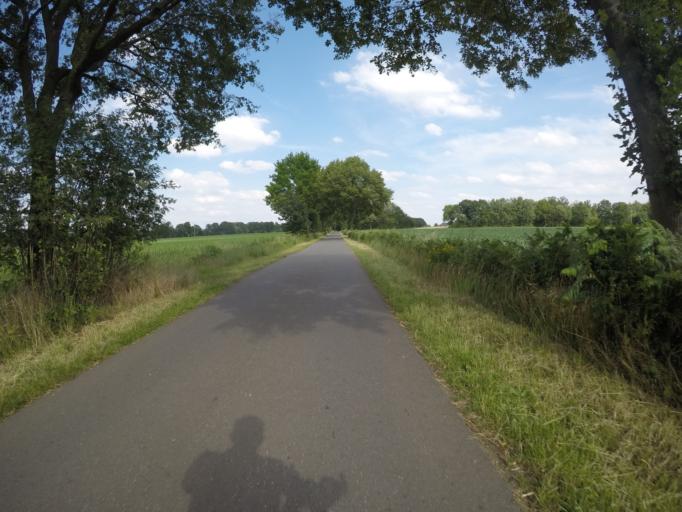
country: DE
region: North Rhine-Westphalia
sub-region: Regierungsbezirk Munster
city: Velen
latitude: 51.8809
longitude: 7.0805
